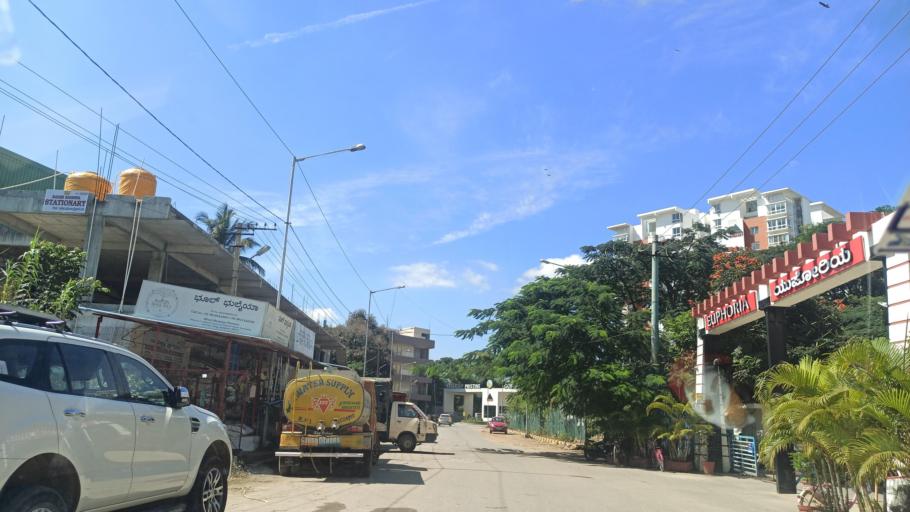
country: IN
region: Karnataka
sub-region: Bangalore Urban
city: Bangalore
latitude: 12.9267
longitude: 77.6632
